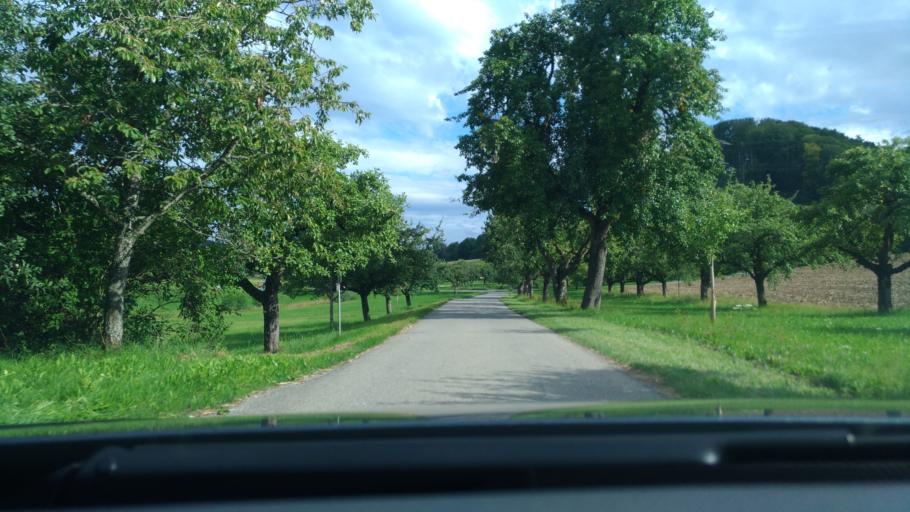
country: DE
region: Baden-Wuerttemberg
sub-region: Tuebingen Region
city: Sipplingen
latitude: 47.8162
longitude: 9.1105
